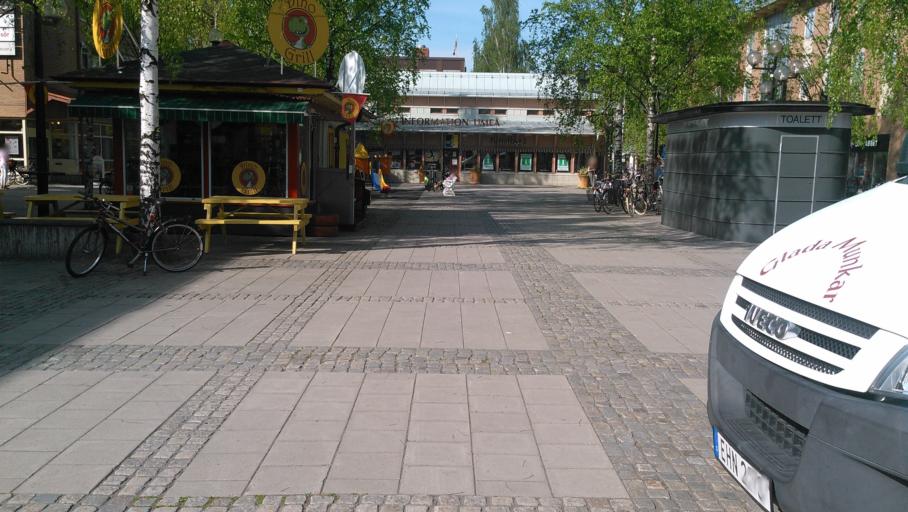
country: SE
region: Vaesterbotten
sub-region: Umea Kommun
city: Umea
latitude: 63.8264
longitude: 20.2604
